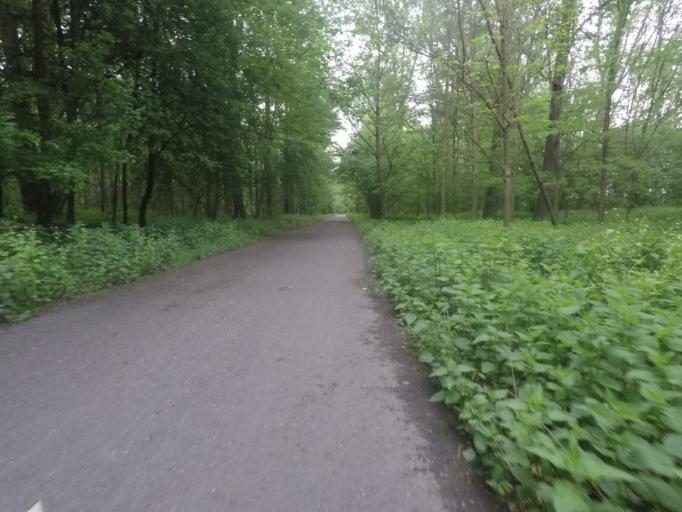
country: DE
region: North Rhine-Westphalia
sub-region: Regierungsbezirk Koln
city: Porz am Rhein
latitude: 50.8862
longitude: 7.0473
